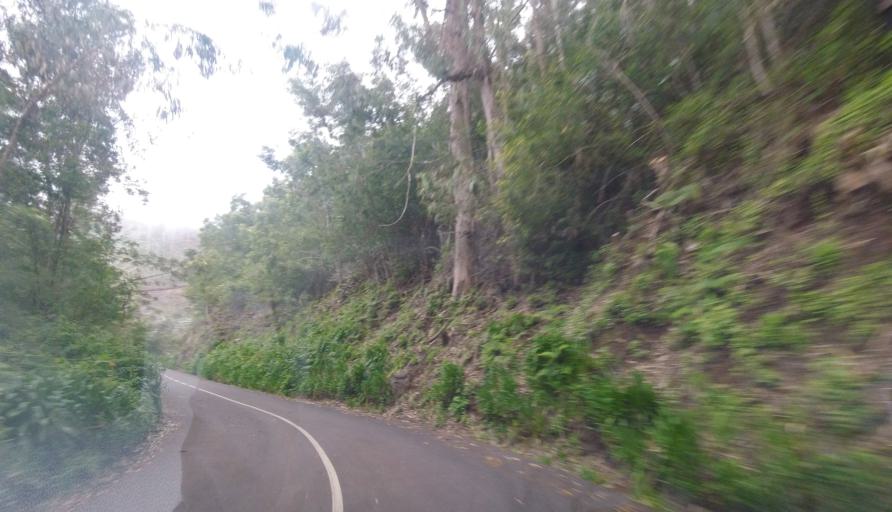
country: PT
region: Madeira
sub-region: Funchal
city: Nossa Senhora do Monte
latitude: 32.6920
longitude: -16.8947
